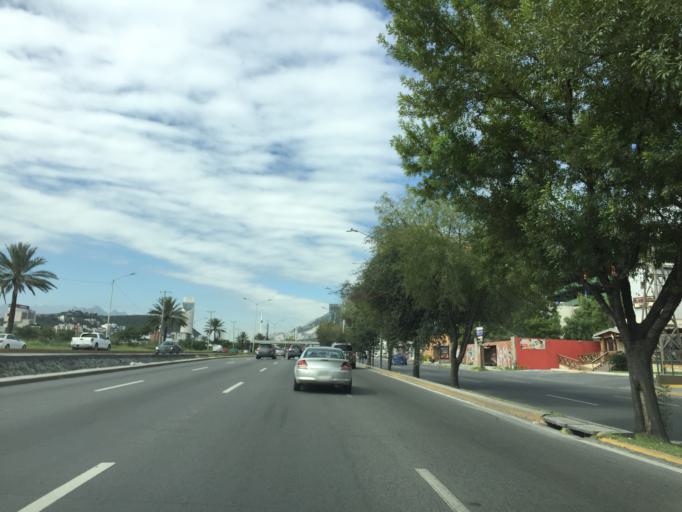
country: MX
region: Nuevo Leon
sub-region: Monterrey
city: Monterrey
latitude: 25.6689
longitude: -100.3393
